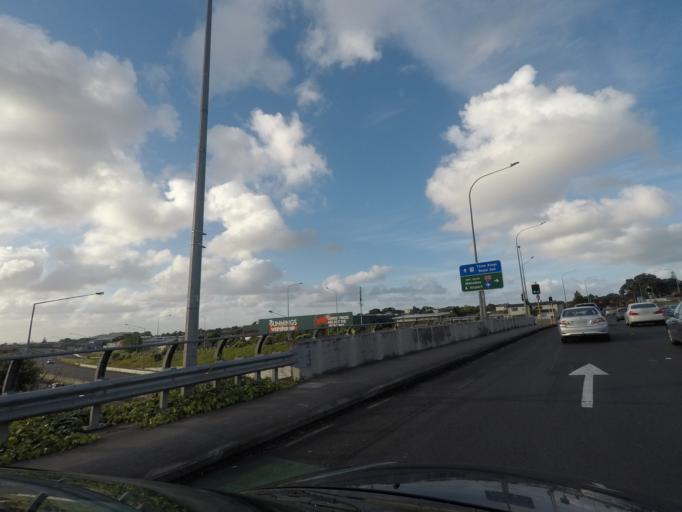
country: NZ
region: Auckland
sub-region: Auckland
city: Auckland
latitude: -36.9180
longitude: 174.7580
